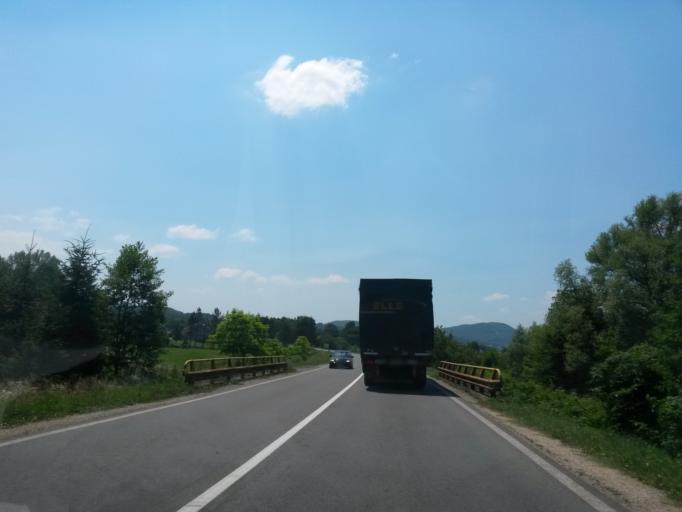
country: BA
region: Federation of Bosnia and Herzegovina
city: Lijesnica
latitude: 44.4843
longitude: 18.0714
